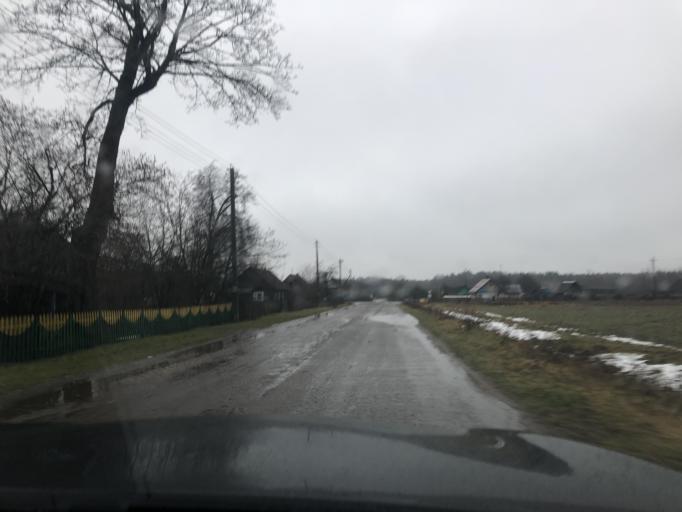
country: BY
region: Grodnenskaya
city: Hal'shany
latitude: 54.1639
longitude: 26.0877
